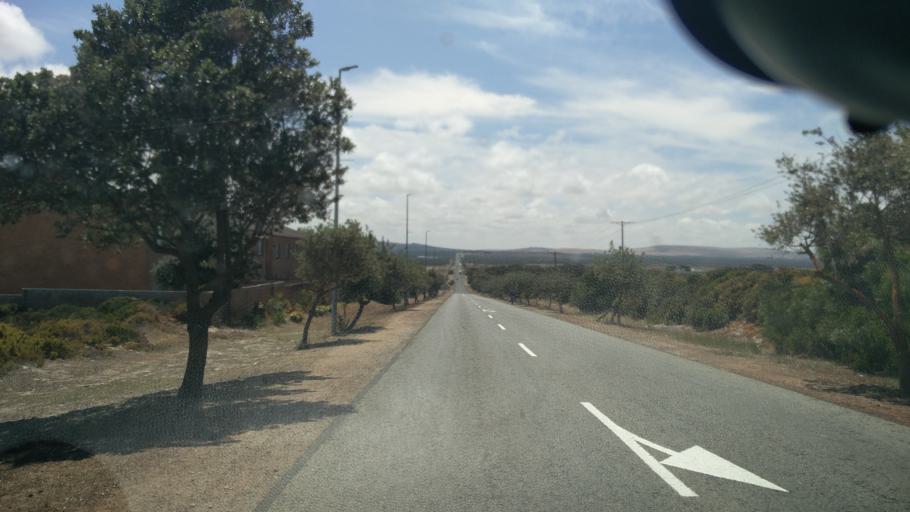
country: ZA
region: Western Cape
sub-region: City of Cape Town
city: Atlantis
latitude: -33.3441
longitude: 18.1644
